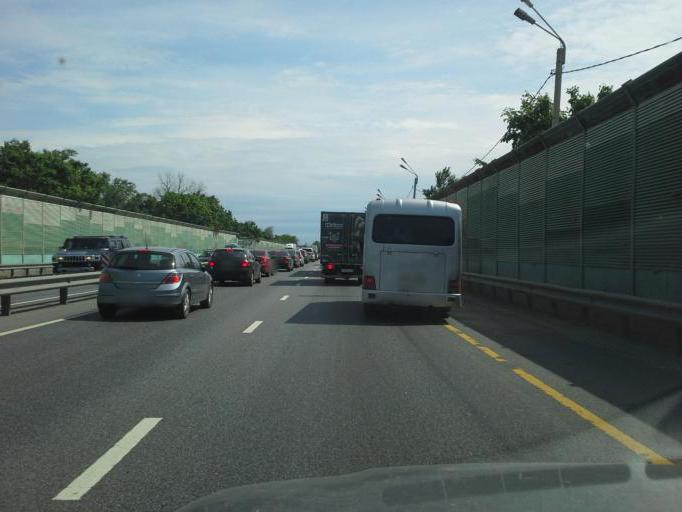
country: RU
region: Moskovskaya
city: Zheleznodorozhnyy
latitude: 55.8039
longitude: 38.0289
